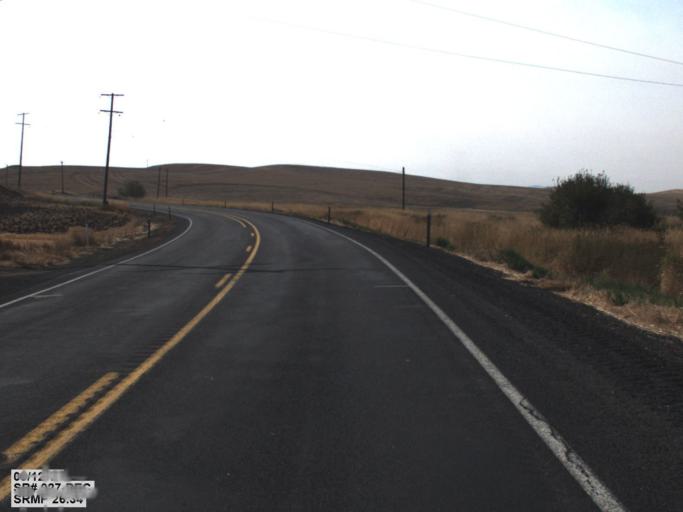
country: US
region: Washington
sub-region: Whitman County
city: Colfax
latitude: 47.0308
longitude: -117.1536
